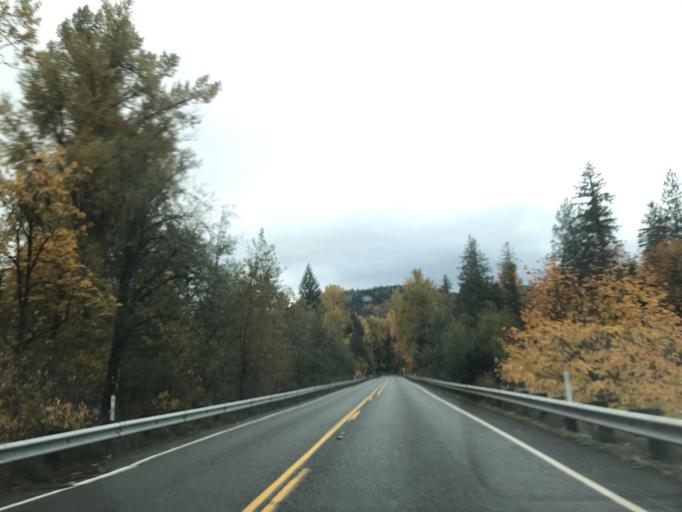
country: US
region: Washington
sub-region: Whatcom County
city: Peaceful Valley
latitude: 48.8187
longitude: -122.1983
